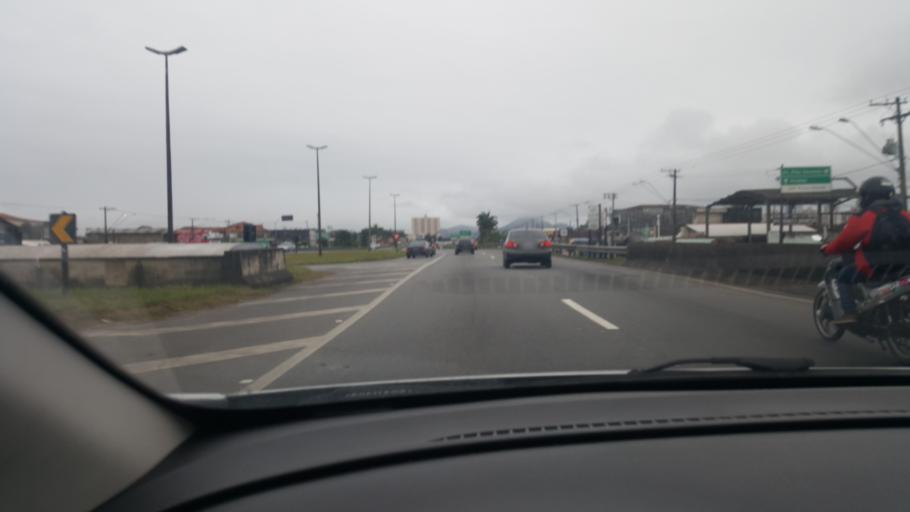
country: BR
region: Sao Paulo
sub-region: Praia Grande
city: Praia Grande
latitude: -24.0177
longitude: -46.4687
